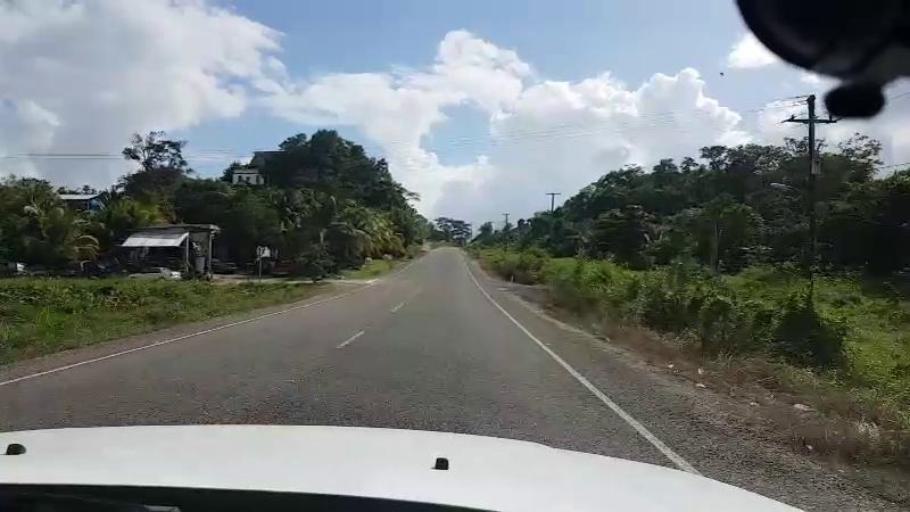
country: BZ
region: Cayo
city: Belmopan
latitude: 17.2340
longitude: -88.7803
